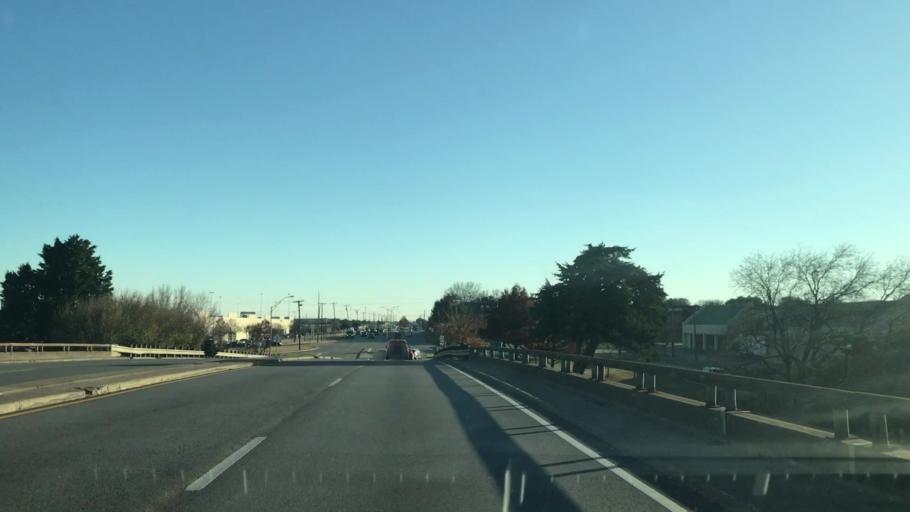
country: US
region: Texas
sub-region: Dallas County
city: Mesquite
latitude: 32.7972
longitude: -96.6683
